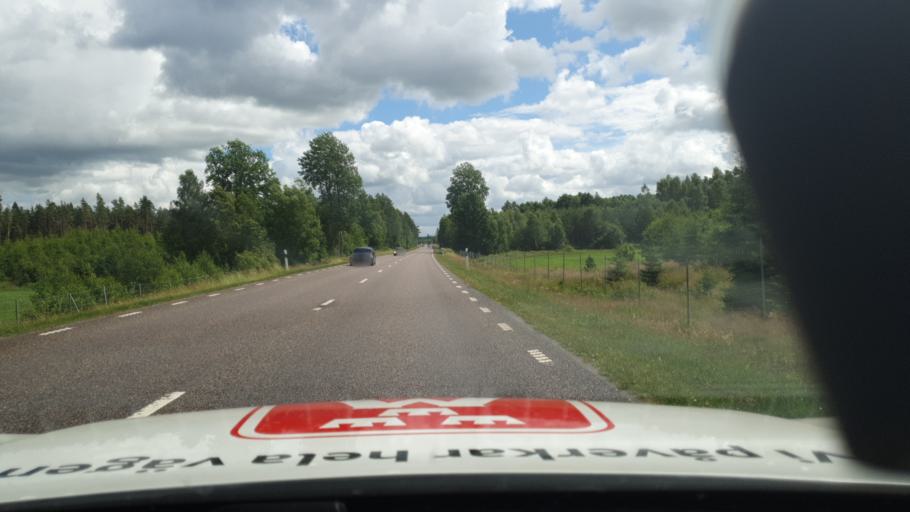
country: SE
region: Vaestra Goetaland
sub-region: Falkopings Kommun
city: Floby
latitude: 58.2015
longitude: 13.3131
